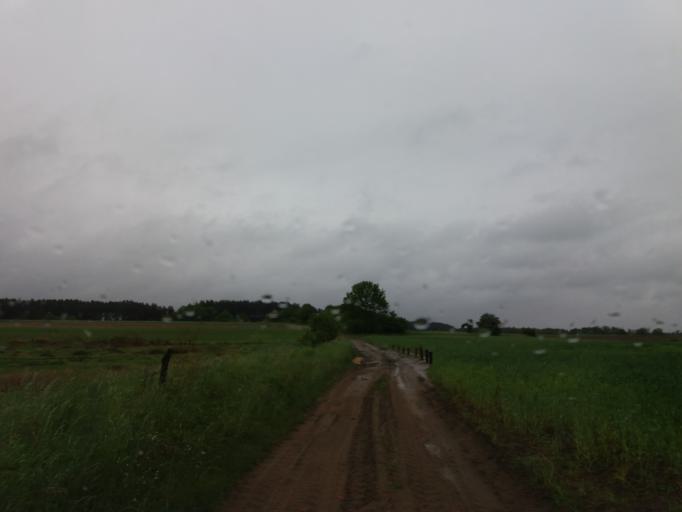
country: PL
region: Lubusz
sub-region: Powiat strzelecko-drezdenecki
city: Dobiegniew
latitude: 53.0182
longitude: 15.8076
